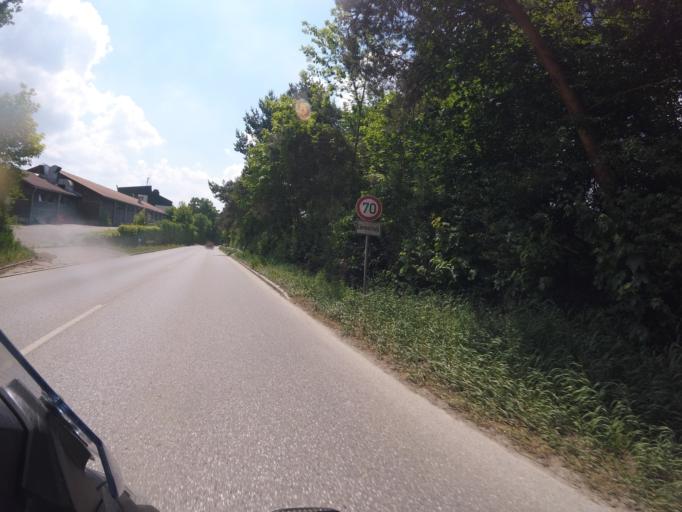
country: DE
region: Bavaria
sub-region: Upper Bavaria
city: Pfaffenhofen an der Ilm
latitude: 48.5385
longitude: 11.4885
